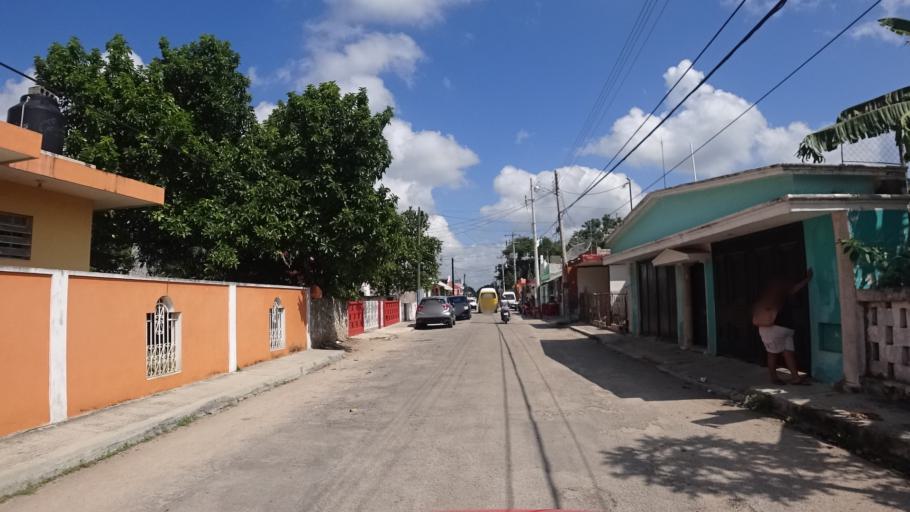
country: MX
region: Yucatan
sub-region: Tizimin
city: Tizimin
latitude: 21.1470
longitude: -88.1530
